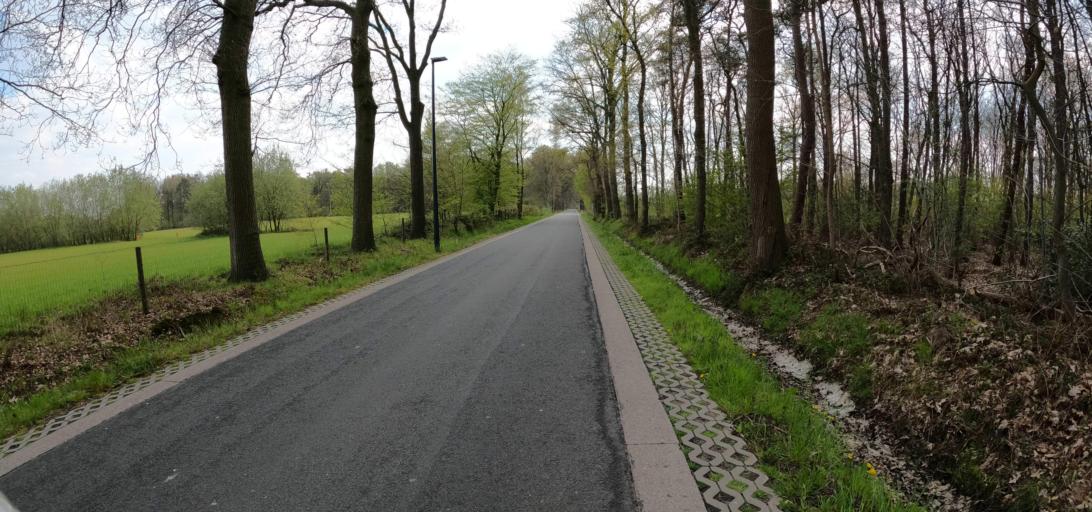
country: BE
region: Flanders
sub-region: Provincie Antwerpen
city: Oostmalle
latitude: 51.2941
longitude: 4.7486
